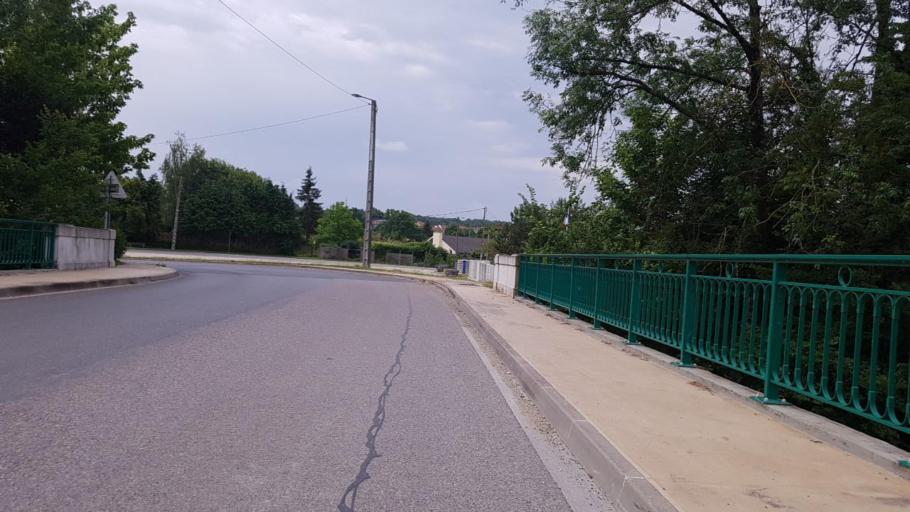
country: FR
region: Champagne-Ardenne
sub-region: Departement de la Marne
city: Sermaize-les-Bains
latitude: 48.7879
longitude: 4.9057
